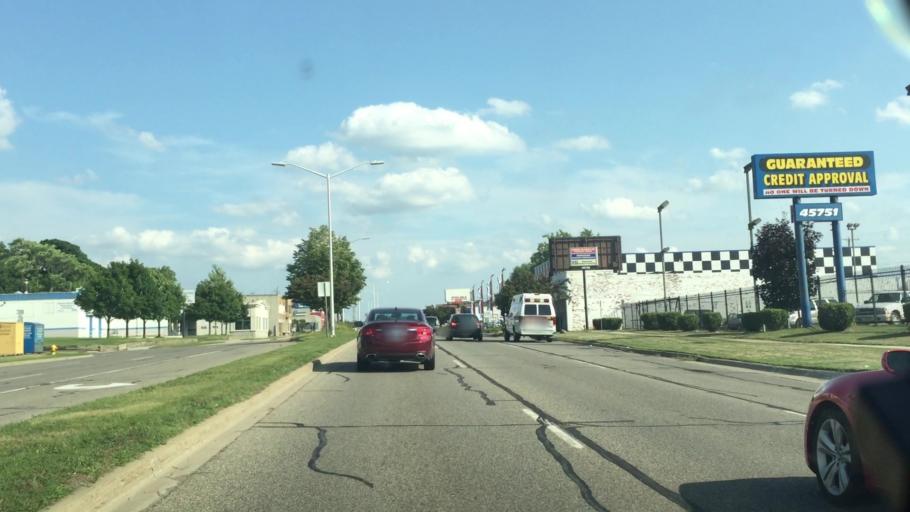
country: US
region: Michigan
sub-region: Oakland County
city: Pontiac
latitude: 42.6267
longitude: -83.2860
